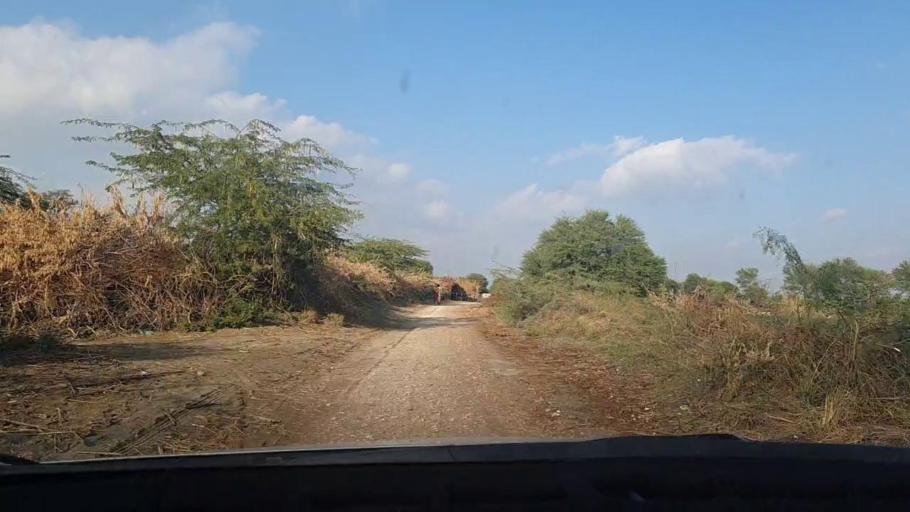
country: PK
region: Sindh
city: Tando Mittha Khan
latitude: 25.8829
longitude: 69.2882
